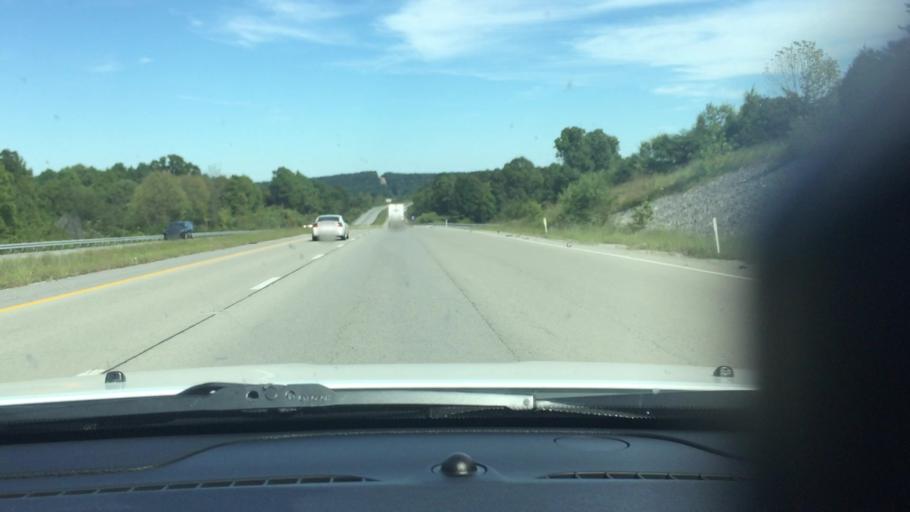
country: US
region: Kentucky
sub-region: Caldwell County
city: Princeton
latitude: 37.1346
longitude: -87.8655
